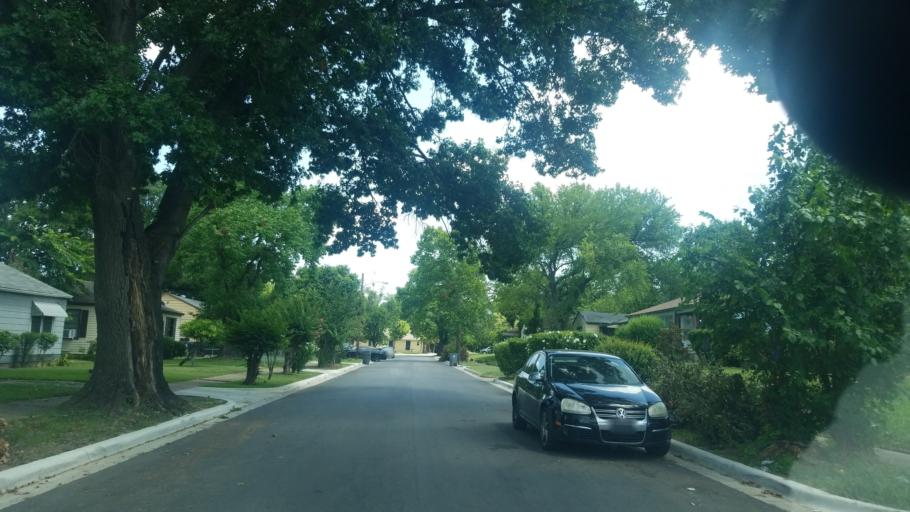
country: US
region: Texas
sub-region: Dallas County
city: Dallas
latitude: 32.7132
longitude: -96.7835
